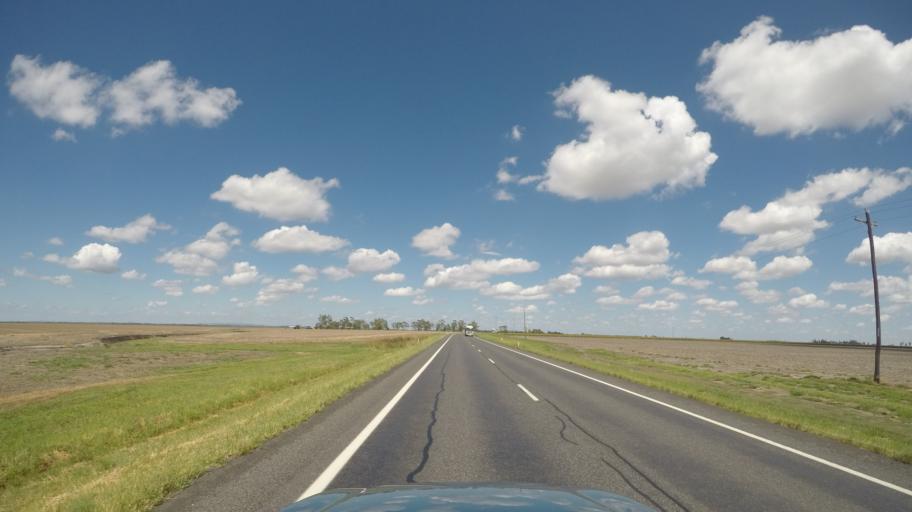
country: AU
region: Queensland
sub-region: Toowoomba
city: Oakey
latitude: -27.7585
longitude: 151.4789
